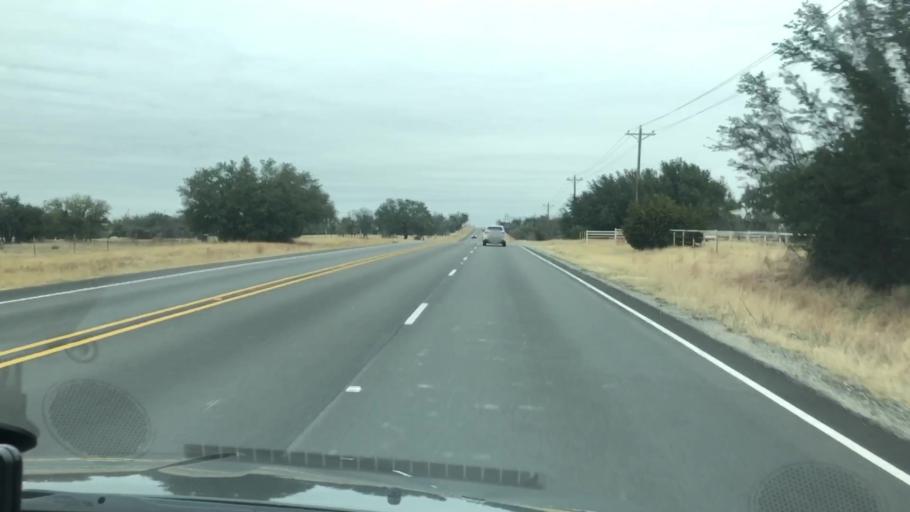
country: US
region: Texas
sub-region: Erath County
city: Stephenville
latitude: 32.3210
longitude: -98.1814
